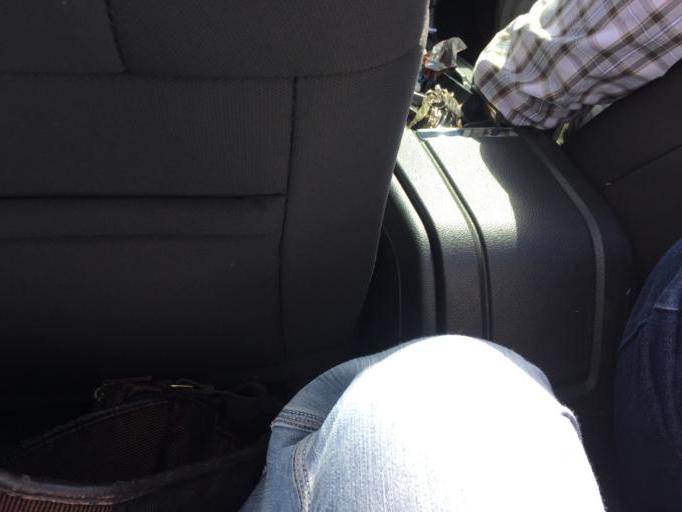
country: DO
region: Santo Domingo
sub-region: Santo Domingo
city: Santo Domingo Este
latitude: 18.4691
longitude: -69.8292
